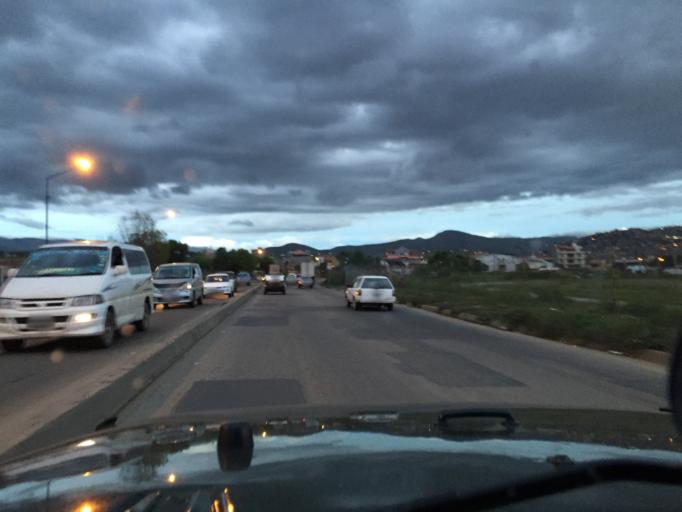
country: BO
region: Cochabamba
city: Cochabamba
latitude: -17.4102
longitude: -66.1693
